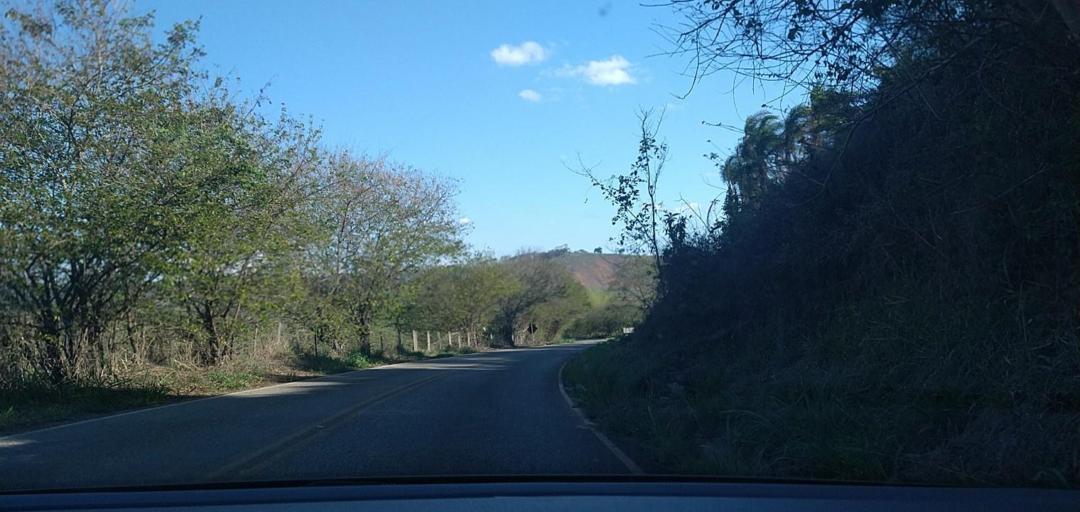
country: BR
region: Minas Gerais
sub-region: Ponte Nova
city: Ponte Nova
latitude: -20.2381
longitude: -42.8979
